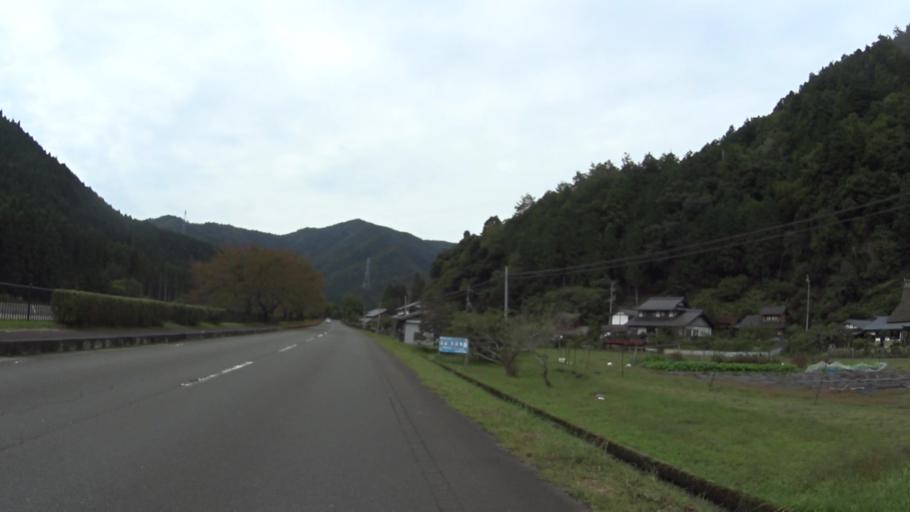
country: JP
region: Fukui
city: Obama
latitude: 35.3104
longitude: 135.6329
